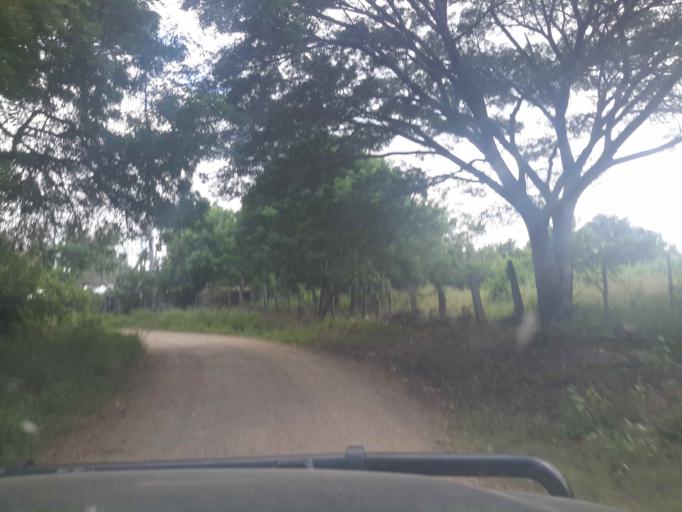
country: NI
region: Granada
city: Nandaime
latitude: 11.6752
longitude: -85.9210
